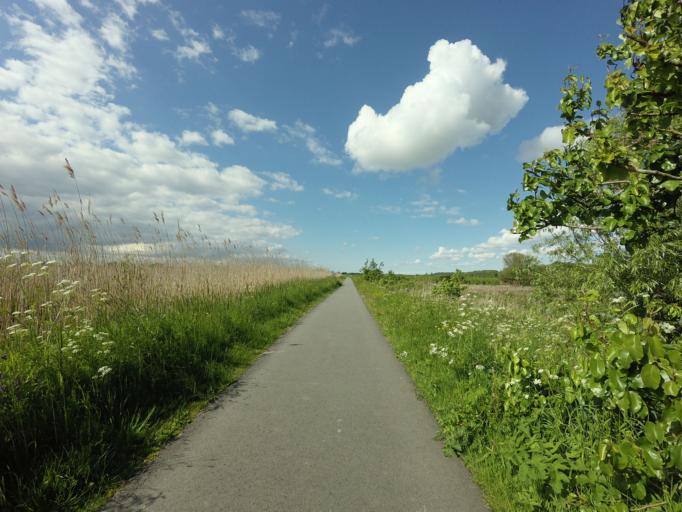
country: NL
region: Utrecht
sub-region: Gemeente Lopik
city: Lopik
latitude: 51.9534
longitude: 4.9911
